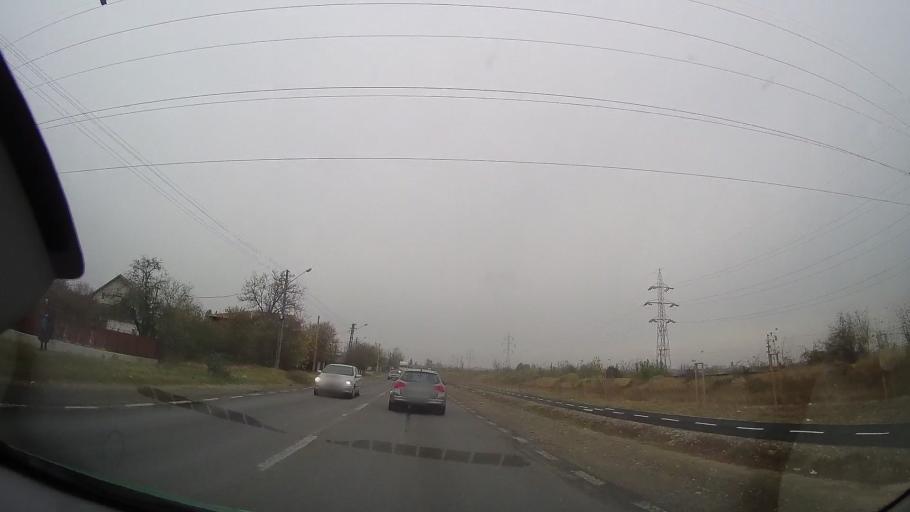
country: RO
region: Prahova
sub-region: Comuna Blejoiu
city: Ploiestiori
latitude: 44.9823
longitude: 26.0161
